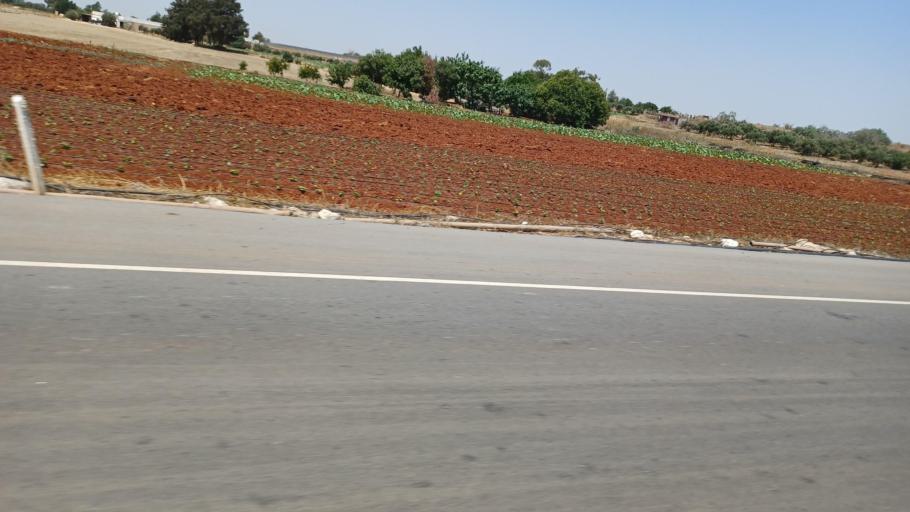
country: CY
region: Ammochostos
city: Liopetri
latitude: 34.9917
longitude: 33.9315
